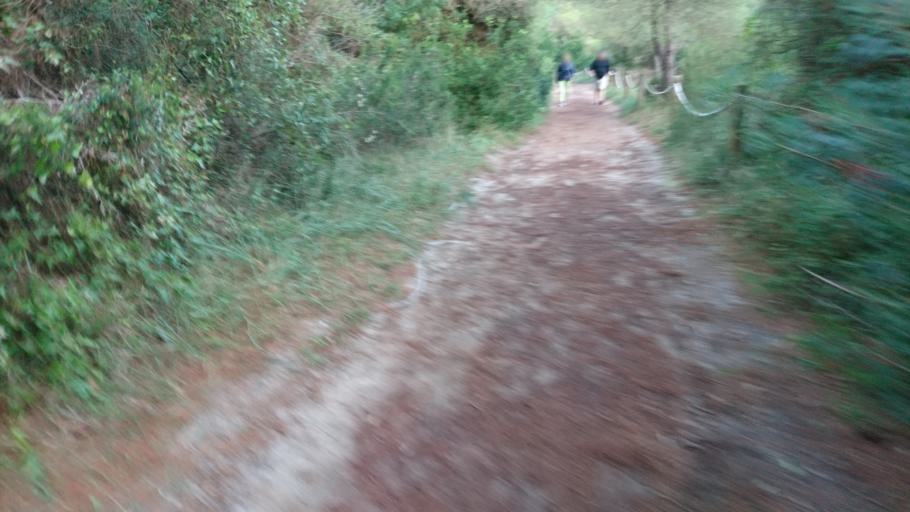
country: ES
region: Balearic Islands
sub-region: Illes Balears
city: Port d'Alcudia
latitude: 39.7840
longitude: 3.1303
